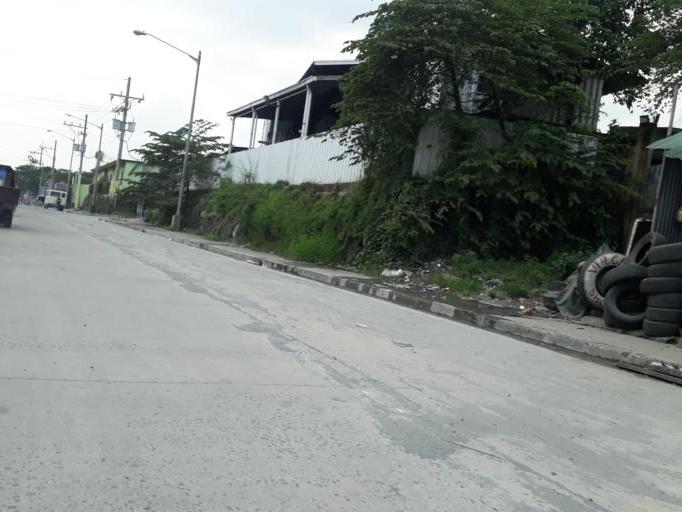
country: PH
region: Calabarzon
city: Bagong Pagasa
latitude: 14.6994
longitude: 121.0164
